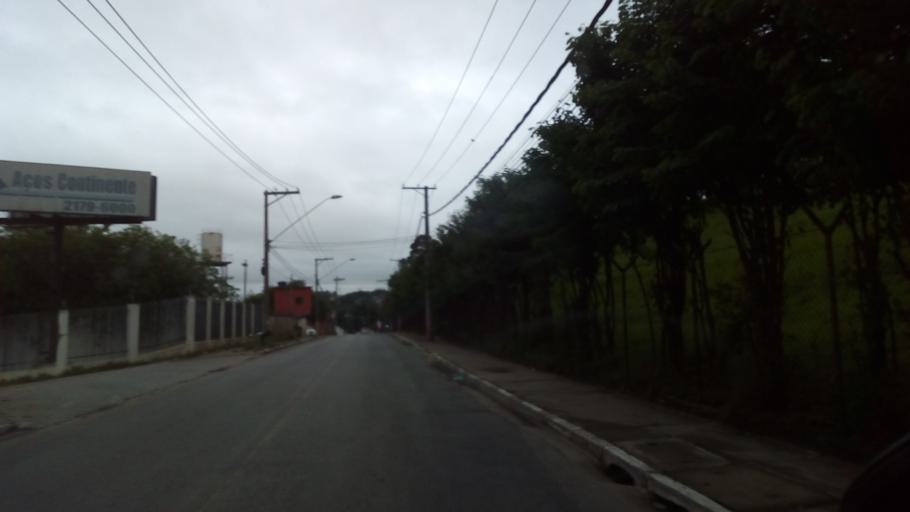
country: BR
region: Sao Paulo
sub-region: Itaquaquecetuba
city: Itaquaquecetuba
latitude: -23.4259
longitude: -46.4125
